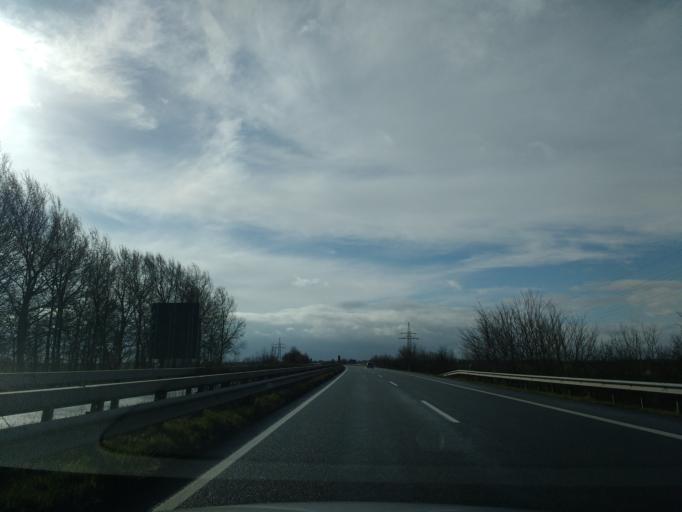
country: DE
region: Lower Saxony
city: Cuxhaven
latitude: 53.8130
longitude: 8.7076
